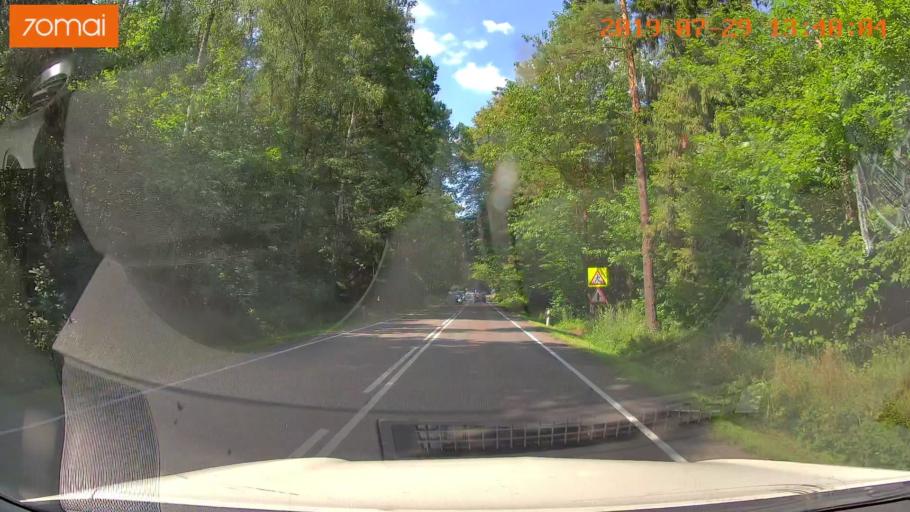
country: RU
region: Kaliningrad
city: Svetlyy
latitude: 54.7261
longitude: 20.1429
